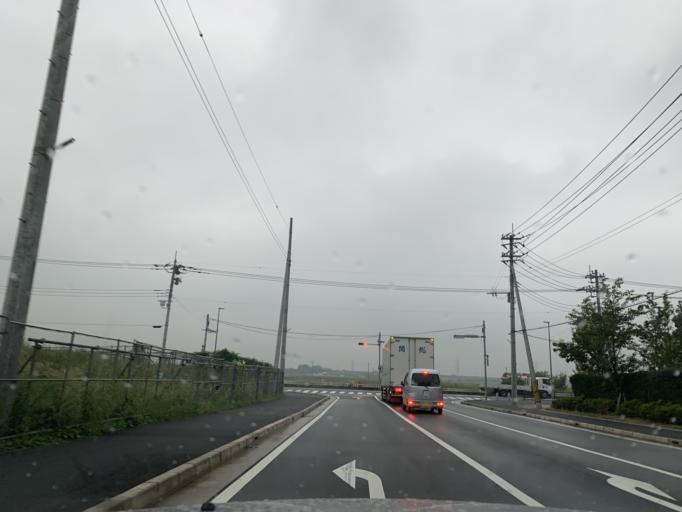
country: JP
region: Chiba
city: Noda
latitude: 35.9091
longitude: 139.8895
